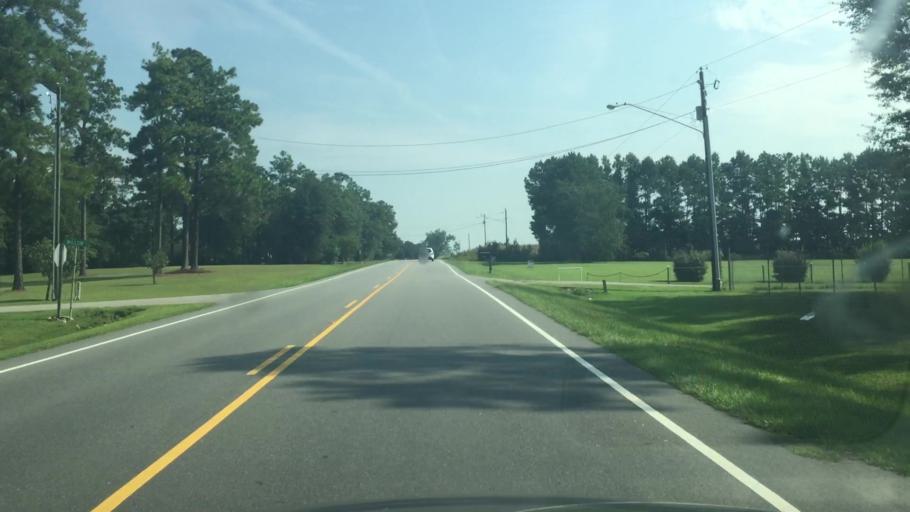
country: US
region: North Carolina
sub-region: Columbus County
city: Tabor City
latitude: 34.1640
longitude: -78.8454
